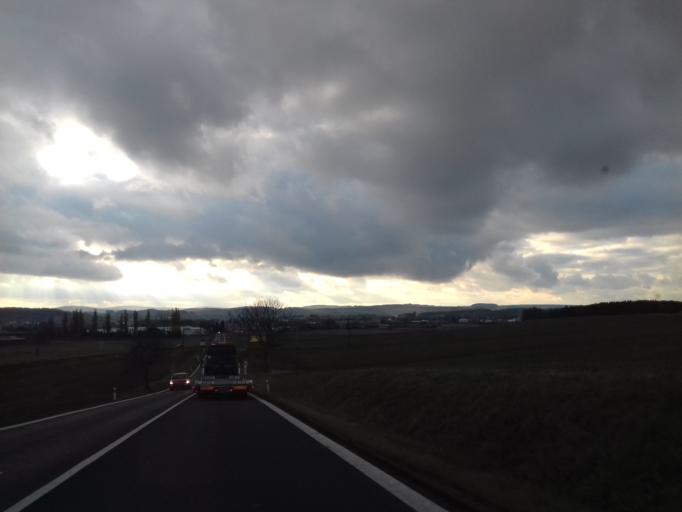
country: CZ
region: Pardubicky
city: Pomezi
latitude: 49.7223
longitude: 16.2958
